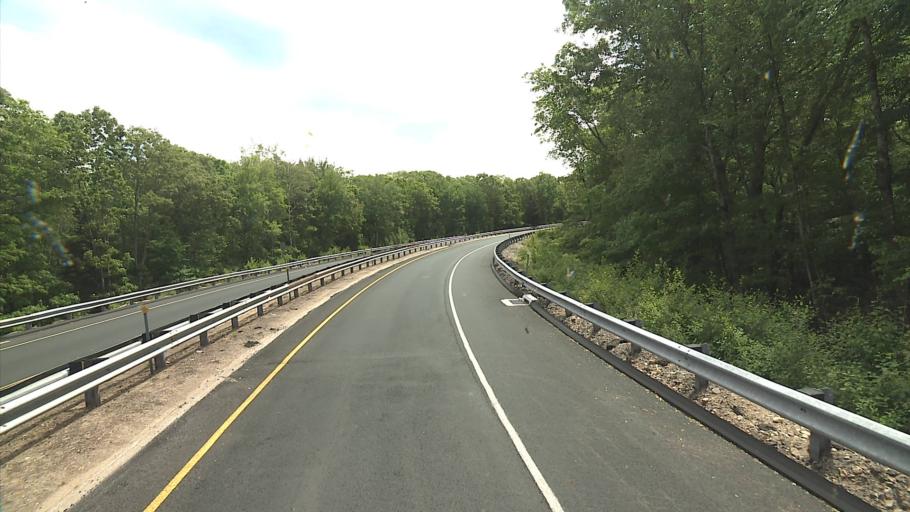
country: US
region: Connecticut
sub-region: New London County
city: Niantic
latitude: 41.3264
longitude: -72.2519
